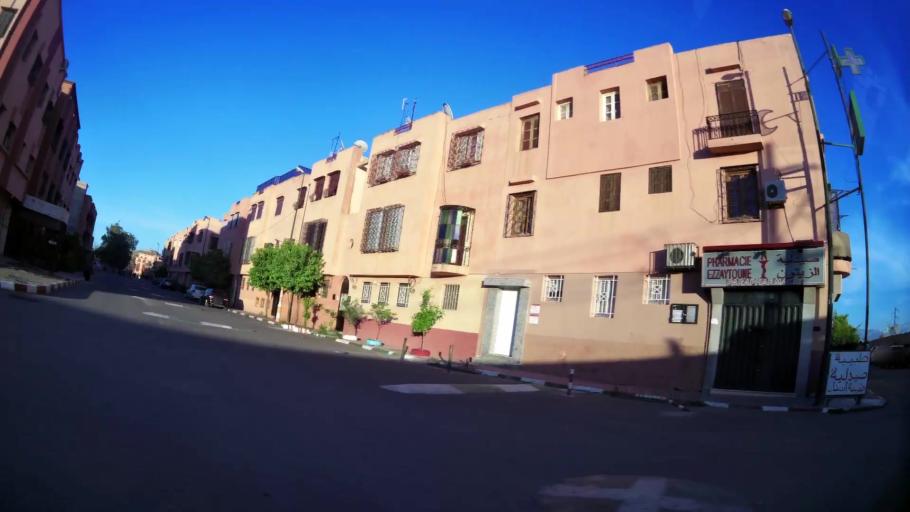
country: MA
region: Marrakech-Tensift-Al Haouz
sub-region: Marrakech
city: Marrakesh
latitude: 31.6395
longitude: -8.0397
